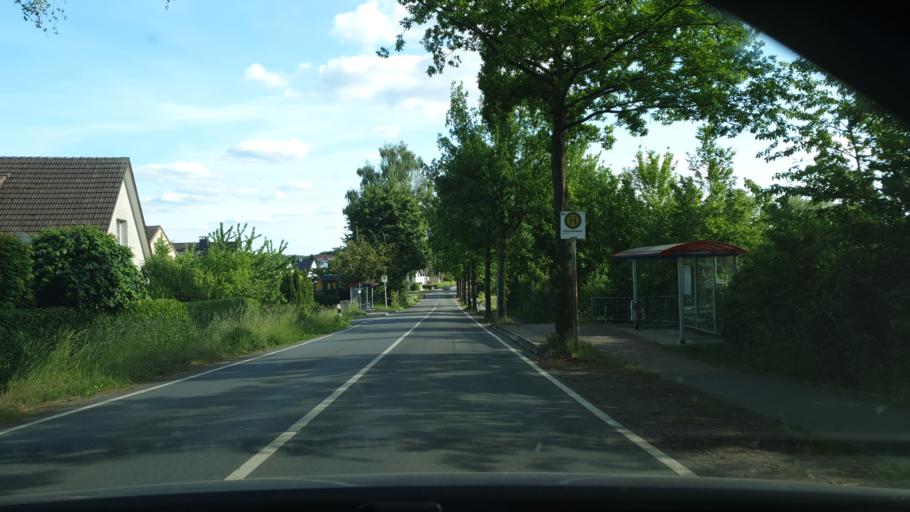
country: DE
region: North Rhine-Westphalia
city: Spenge
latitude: 52.1460
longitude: 8.5149
